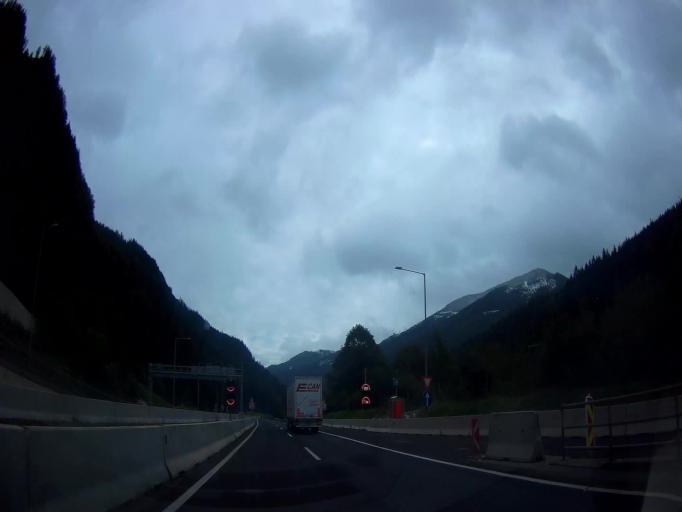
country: AT
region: Styria
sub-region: Politischer Bezirk Leoben
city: Wald am Schoberpass
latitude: 47.4511
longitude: 14.6725
